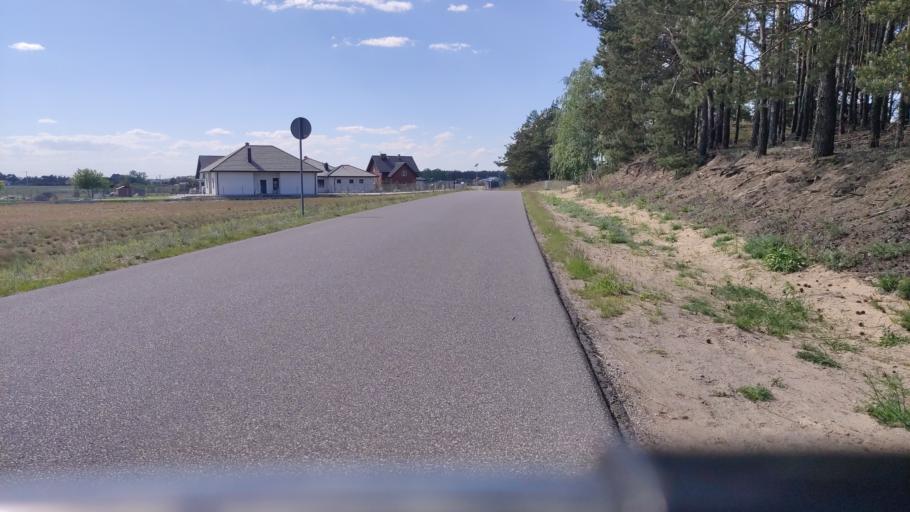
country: PL
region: Kujawsko-Pomorskie
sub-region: Wloclawek
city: Wloclawek
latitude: 52.5840
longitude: 19.0946
